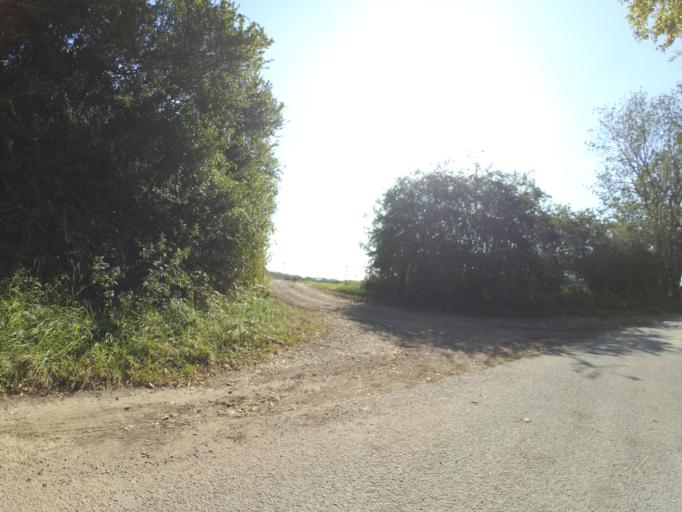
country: GB
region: England
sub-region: Warwickshire
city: Rugby
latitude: 52.4155
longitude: -1.2652
